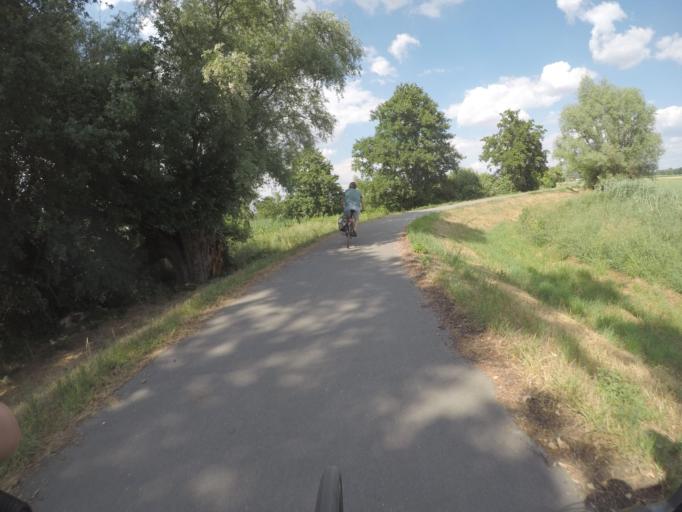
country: DE
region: Brandenburg
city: Ketzin
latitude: 52.4664
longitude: 12.8141
